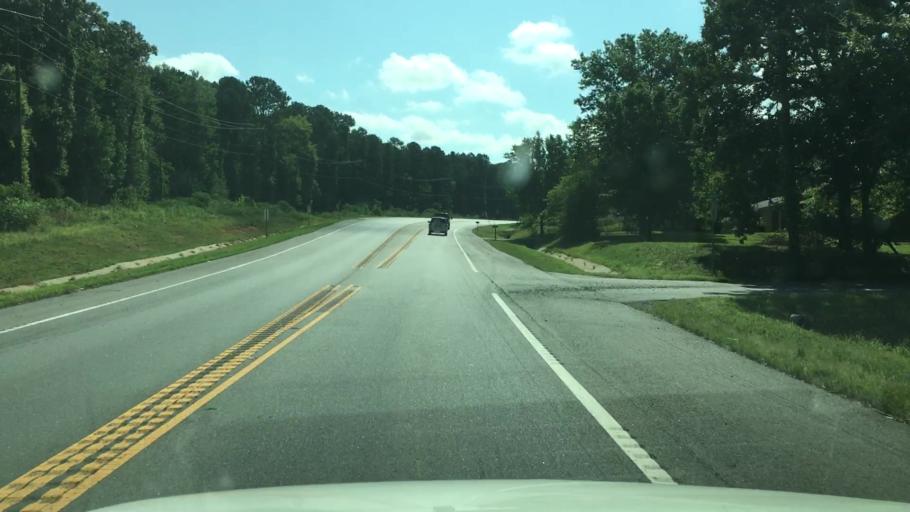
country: US
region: Arkansas
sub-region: Garland County
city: Piney
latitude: 34.5099
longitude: -93.1957
